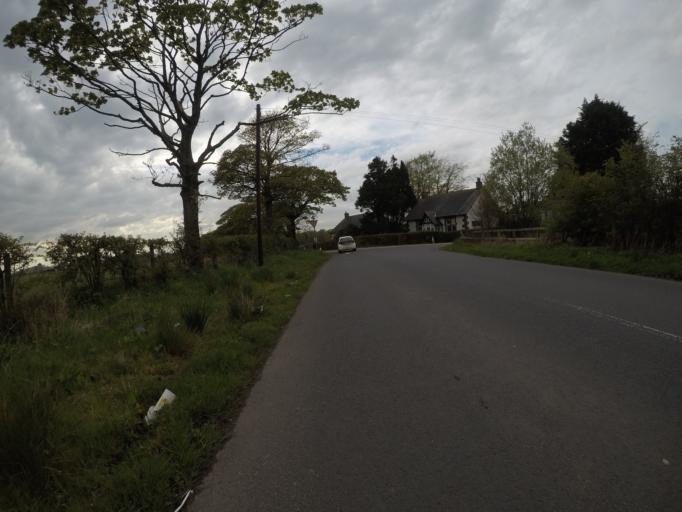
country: GB
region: Scotland
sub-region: East Ayrshire
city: Kilmarnock
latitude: 55.6456
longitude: -4.4846
